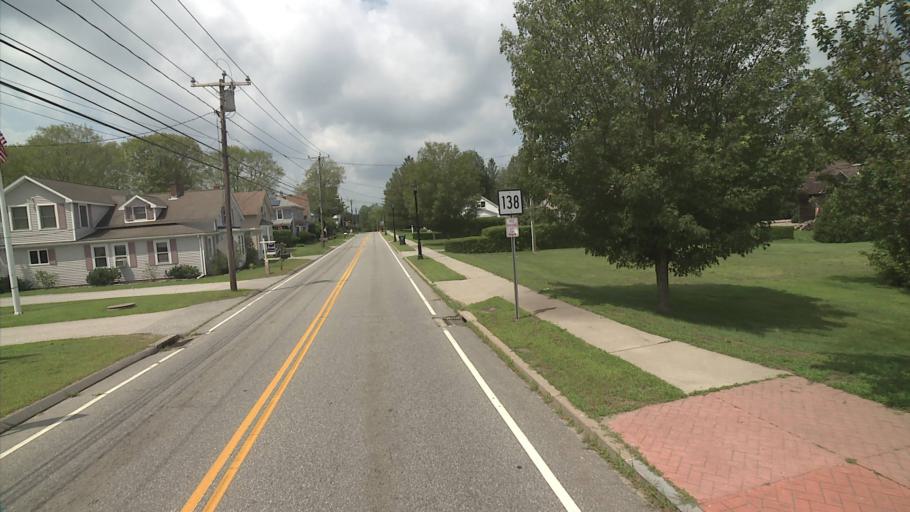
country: US
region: Connecticut
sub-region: Windham County
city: Plainfield
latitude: 41.5729
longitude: -71.8694
